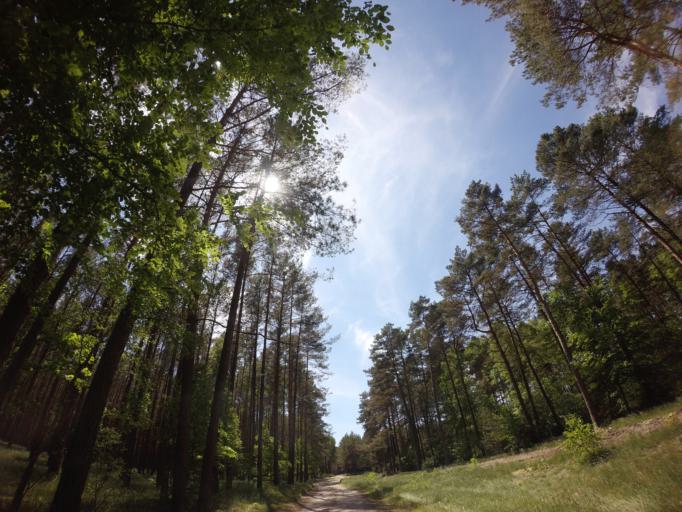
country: PL
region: West Pomeranian Voivodeship
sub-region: Powiat choszczenski
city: Drawno
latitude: 53.1261
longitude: 15.8315
